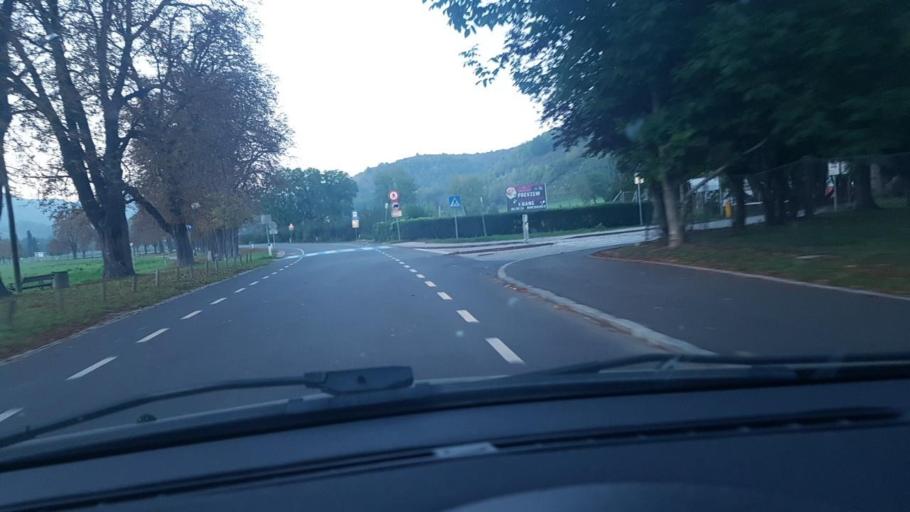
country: SI
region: Maribor
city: Maribor
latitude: 46.5669
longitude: 15.6323
